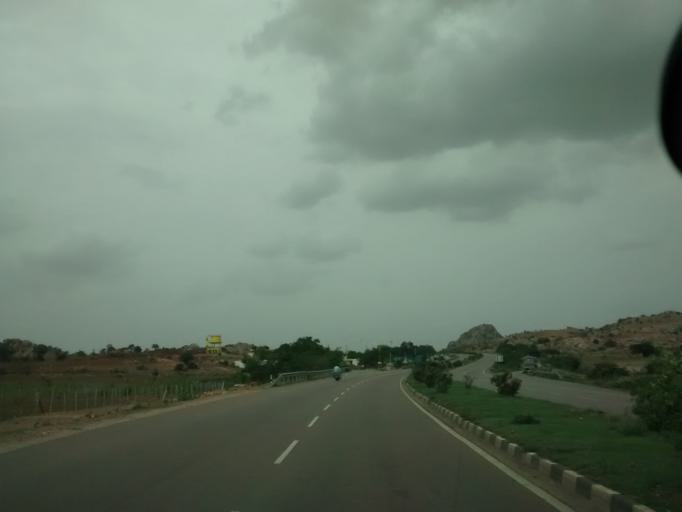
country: IN
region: Andhra Pradesh
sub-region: Kurnool
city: Ramapuram
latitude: 15.1576
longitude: 77.6697
